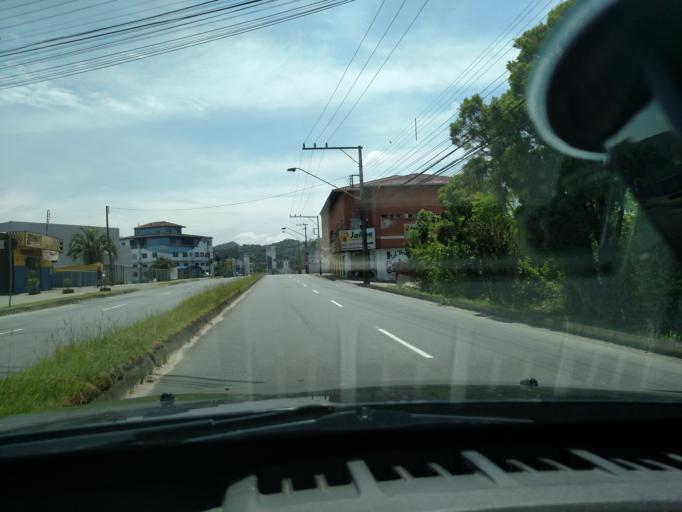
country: BR
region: Santa Catarina
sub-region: Blumenau
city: Blumenau
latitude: -26.8963
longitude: -49.0704
